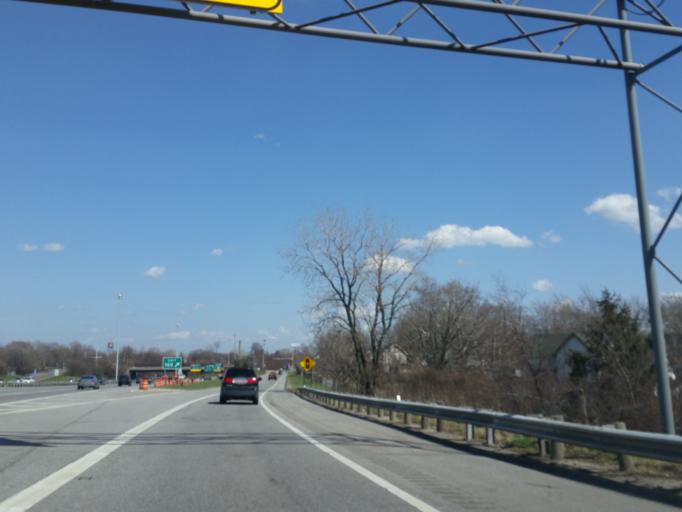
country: US
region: Ohio
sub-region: Cuyahoga County
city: Cleveland
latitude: 41.4747
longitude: -81.7214
